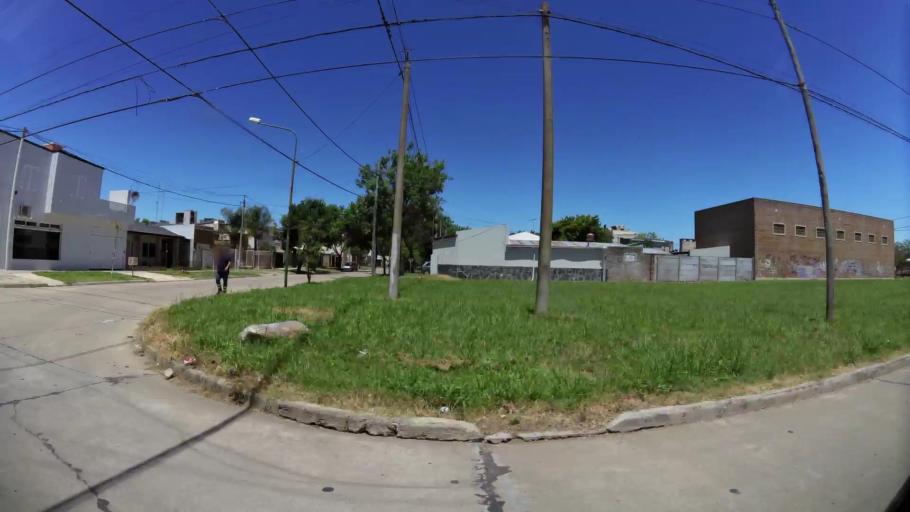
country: AR
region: Santa Fe
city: Rafaela
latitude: -31.2513
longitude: -61.4603
